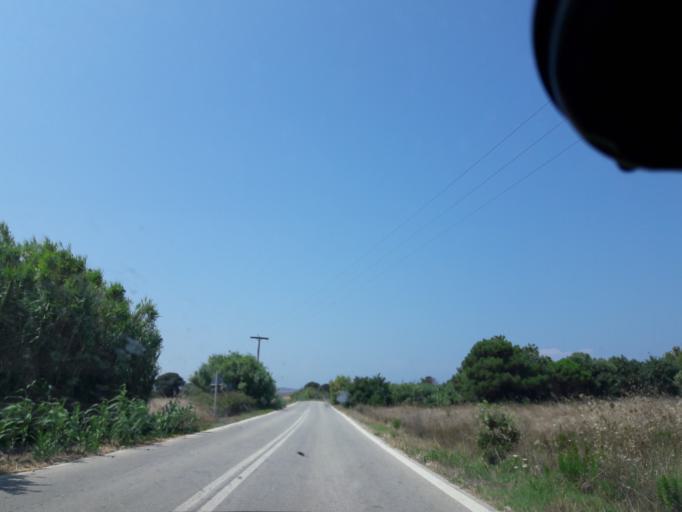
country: GR
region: North Aegean
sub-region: Nomos Lesvou
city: Myrina
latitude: 39.9278
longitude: 25.2965
